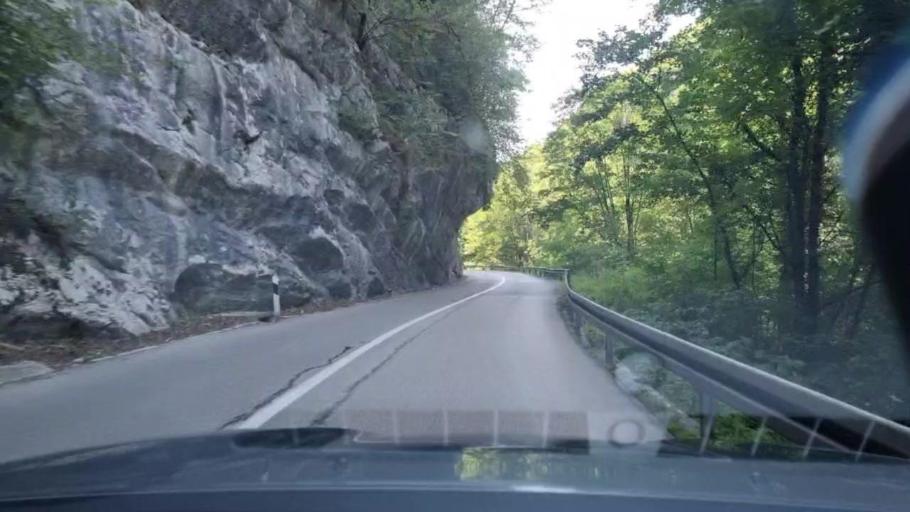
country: BA
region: Federation of Bosnia and Herzegovina
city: Bosanska Krupa
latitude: 44.8718
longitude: 16.0842
